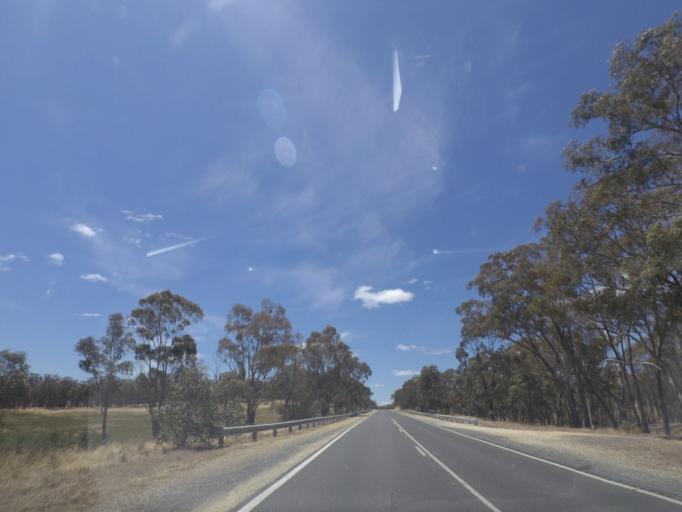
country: AU
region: Victoria
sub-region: Mount Alexander
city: Castlemaine
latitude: -37.1654
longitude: 144.1497
